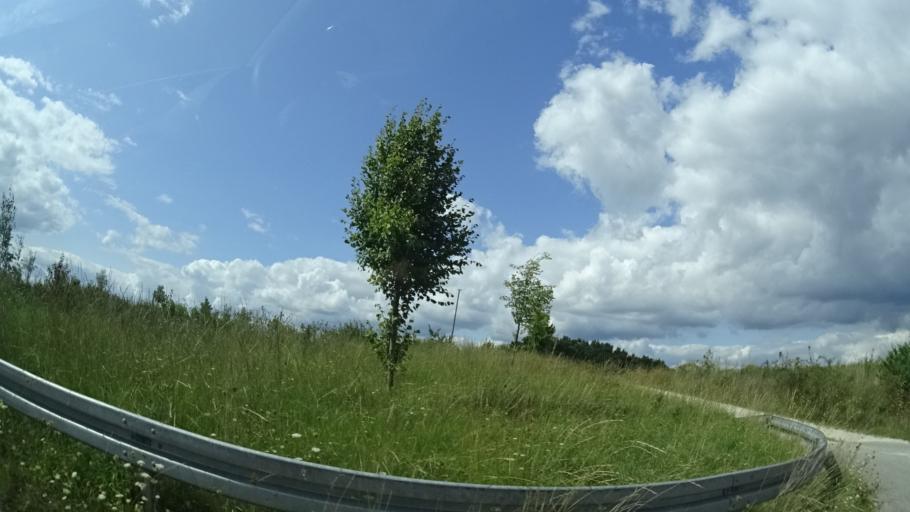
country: DE
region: Bavaria
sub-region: Upper Franconia
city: Untersiemau
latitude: 50.1777
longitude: 10.9836
